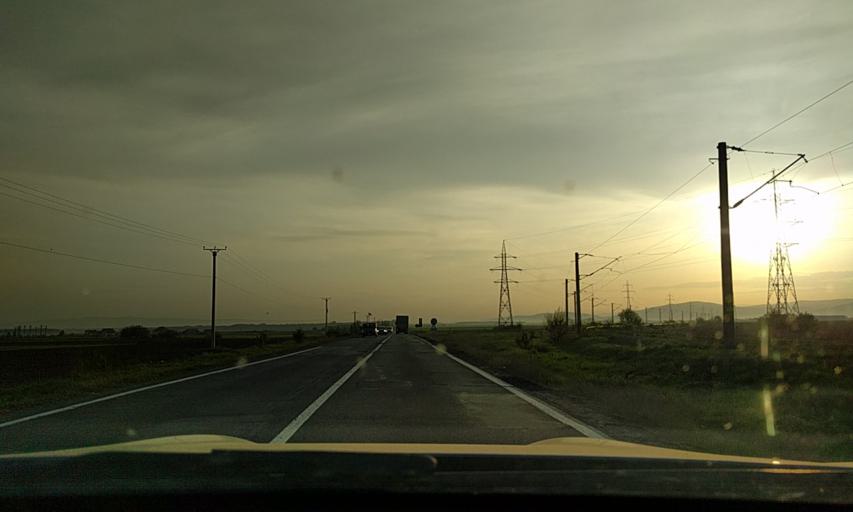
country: RO
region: Brasov
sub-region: Comuna Harman
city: Harman
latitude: 45.7137
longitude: 25.7111
